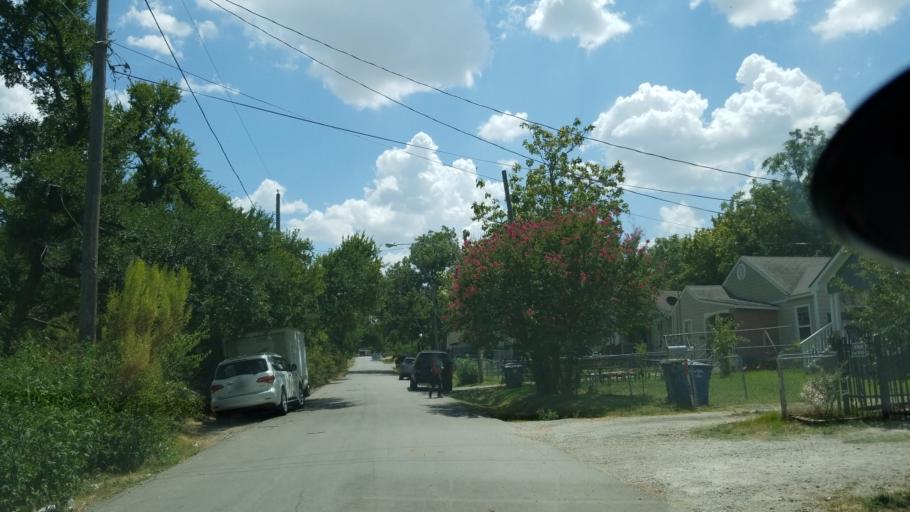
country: US
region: Texas
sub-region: Dallas County
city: Cockrell Hill
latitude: 32.7479
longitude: -96.9062
